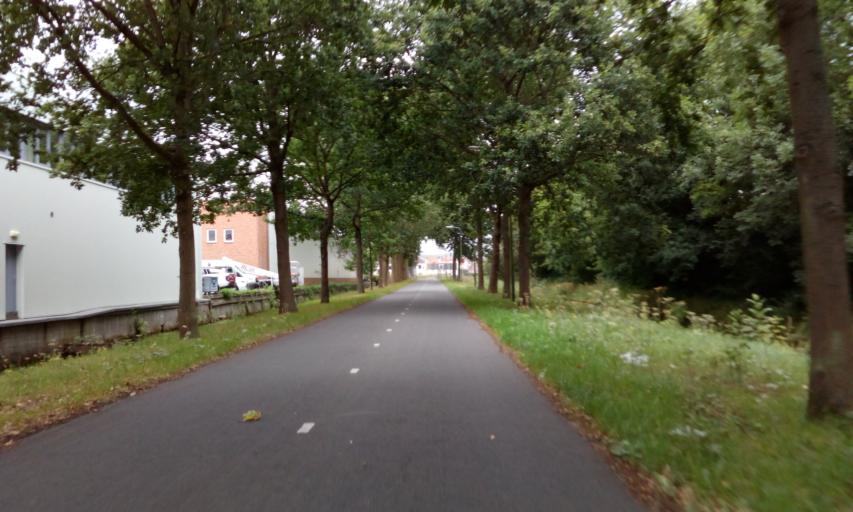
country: NL
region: South Holland
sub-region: Gemeente Leidschendam-Voorburg
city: Voorburg
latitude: 52.0650
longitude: 4.3686
